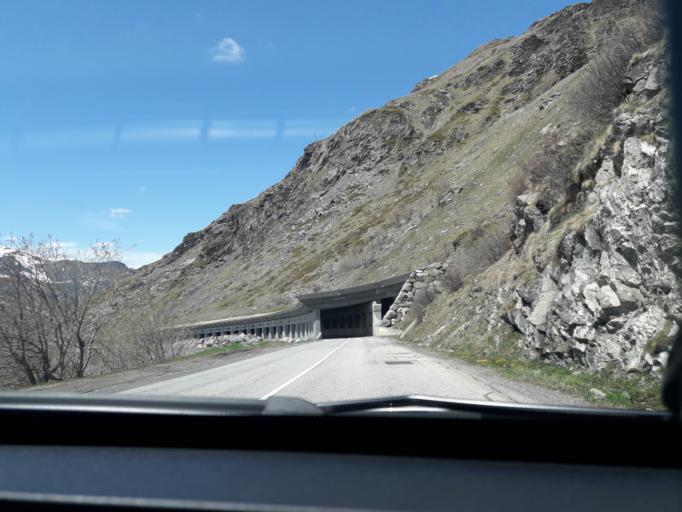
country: FR
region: Rhone-Alpes
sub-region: Departement de la Savoie
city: Val Thorens
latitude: 45.3001
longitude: 6.5636
